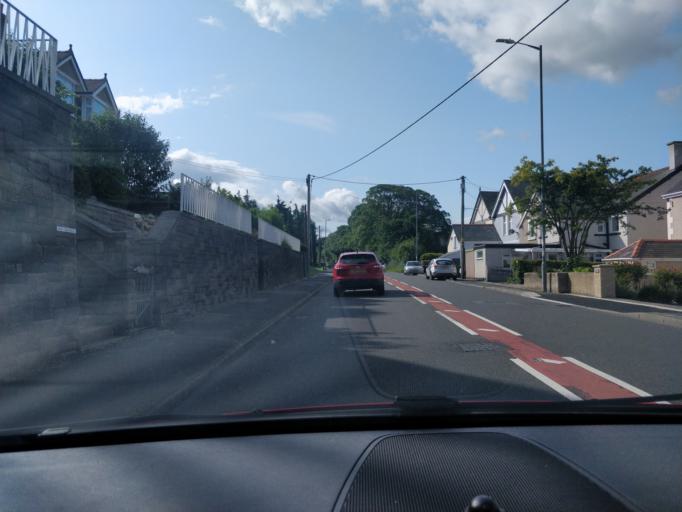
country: GB
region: Wales
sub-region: Conwy
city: Llansantffraid Glan Conwy
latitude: 53.2636
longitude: -3.7997
